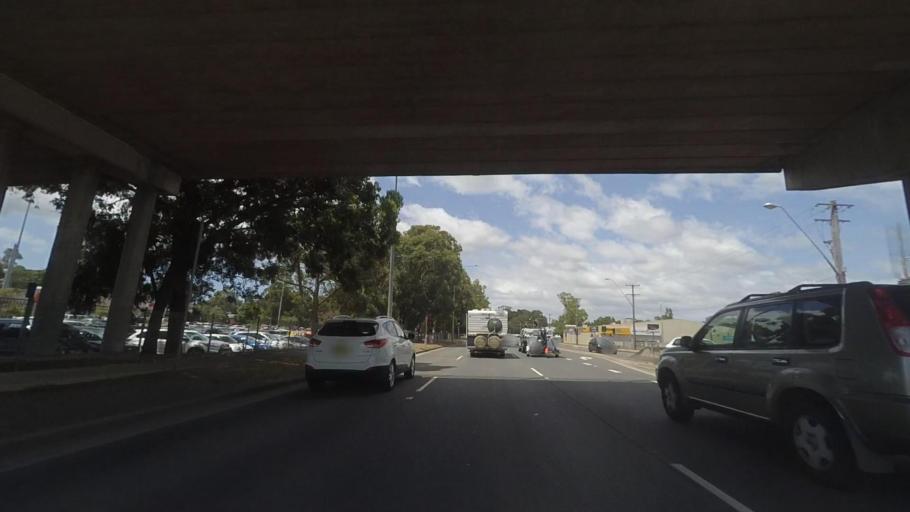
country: AU
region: New South Wales
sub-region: Shoalhaven Shire
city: Nowra
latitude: -34.8761
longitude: 150.6054
